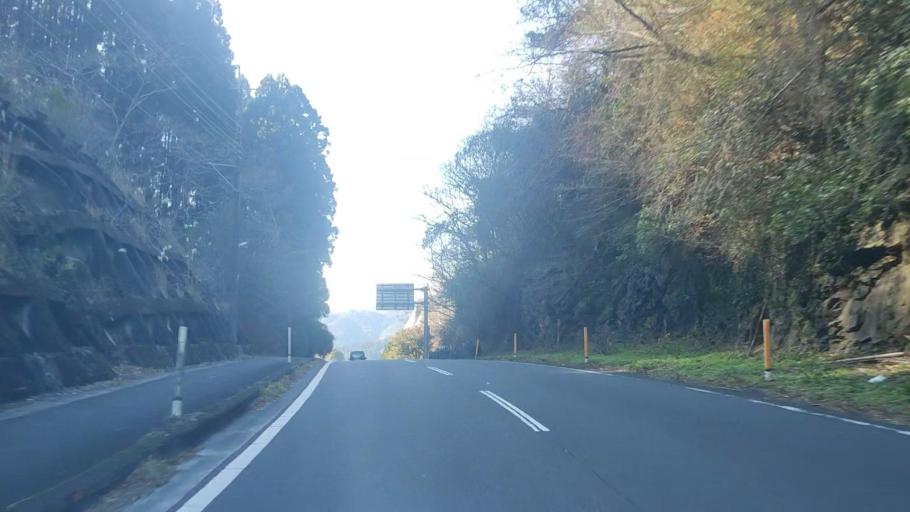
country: JP
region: Oita
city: Saiki
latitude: 32.9750
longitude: 131.8605
